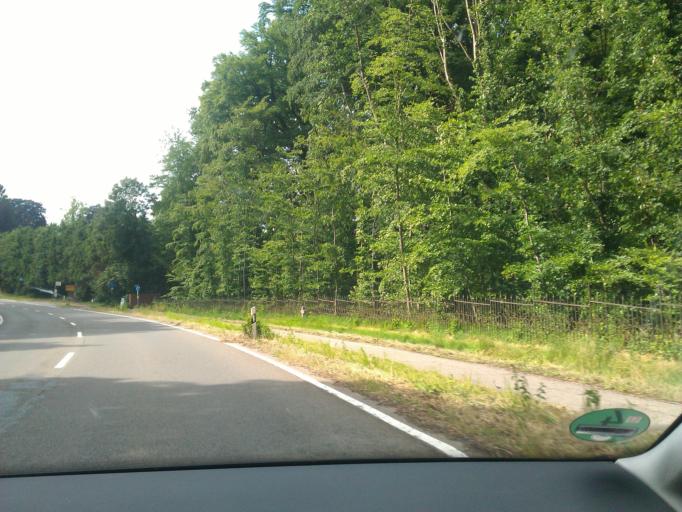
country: DE
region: North Rhine-Westphalia
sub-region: Regierungsbezirk Koln
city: Aachen
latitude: 50.7389
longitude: 6.0906
